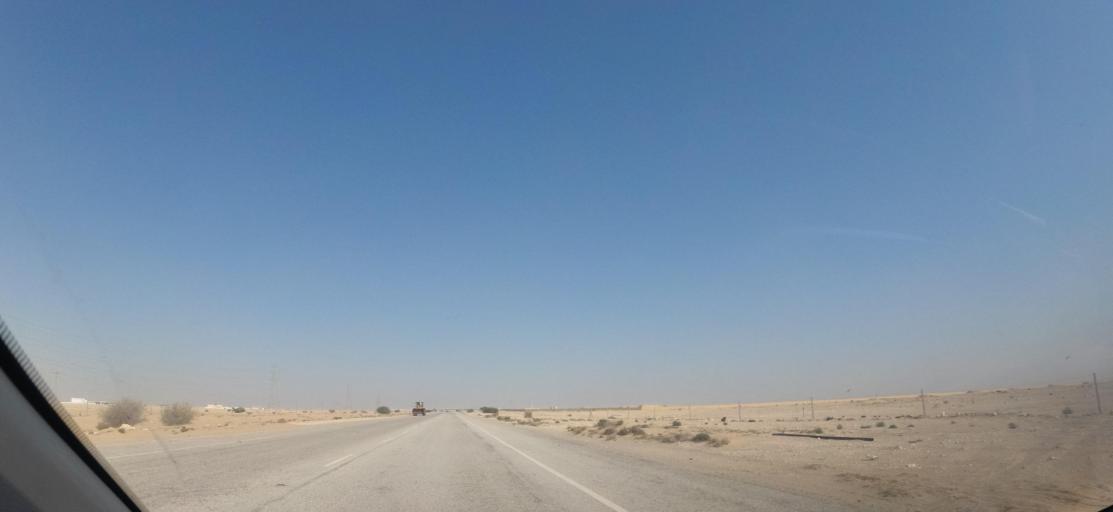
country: QA
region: Baladiyat ar Rayyan
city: Dukhan
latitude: 25.4809
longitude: 50.9604
